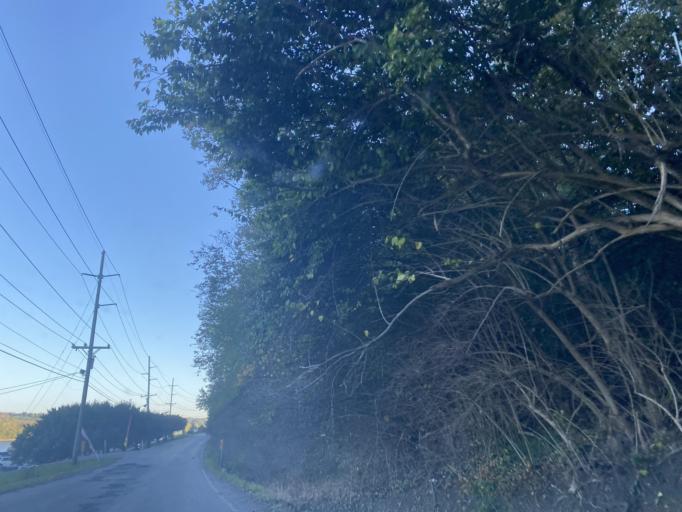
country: US
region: Kentucky
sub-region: Campbell County
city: Dayton
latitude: 39.1096
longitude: -84.4482
